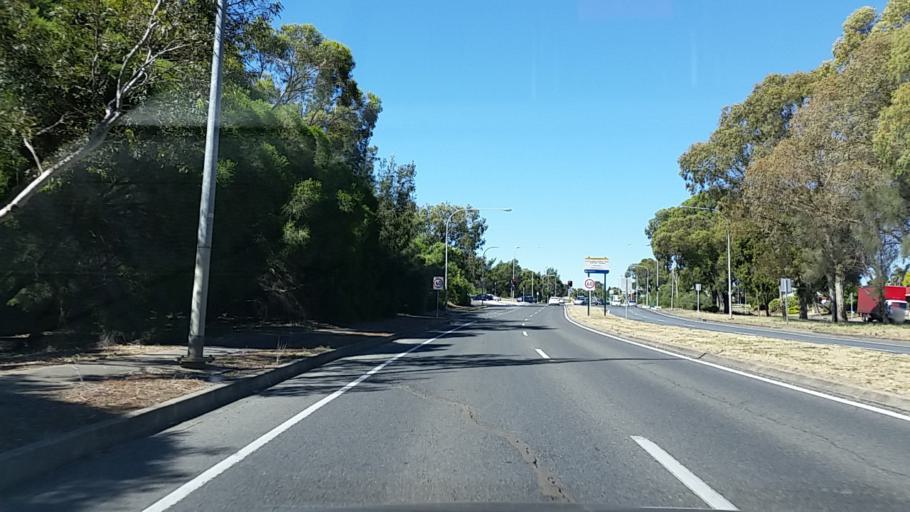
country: AU
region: South Australia
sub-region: Tea Tree Gully
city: Hope Valley
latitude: -34.8081
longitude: 138.6982
